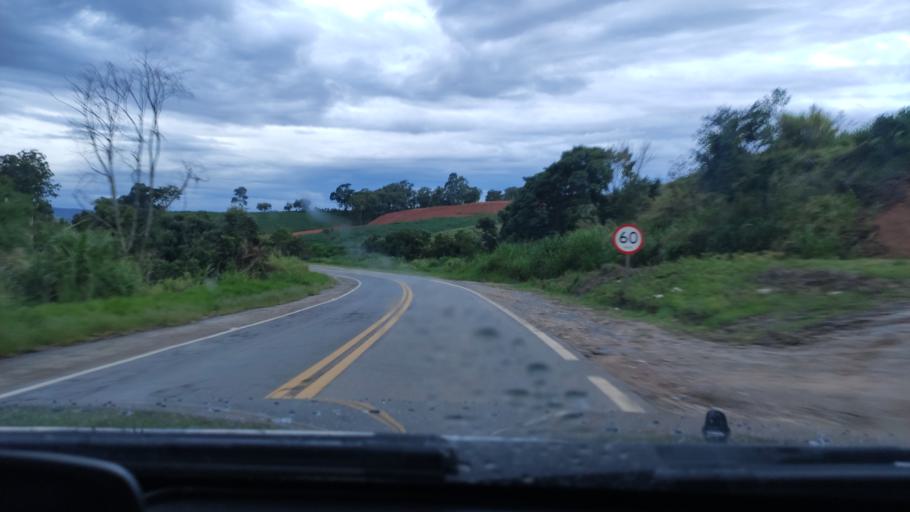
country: BR
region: Sao Paulo
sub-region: Socorro
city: Socorro
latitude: -22.7194
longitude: -46.5642
